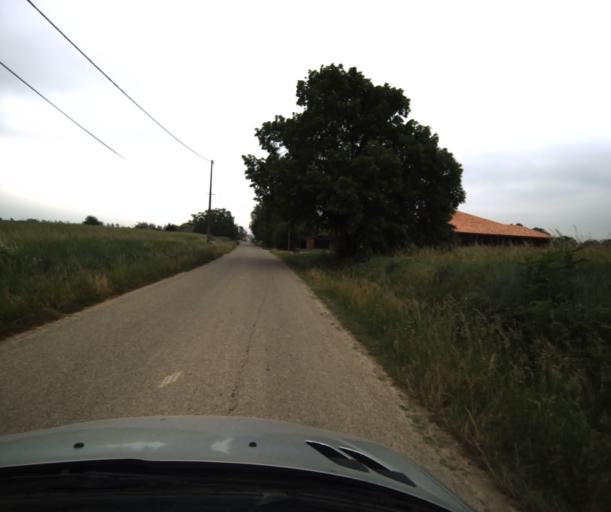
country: FR
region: Midi-Pyrenees
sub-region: Departement du Tarn-et-Garonne
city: Saint-Nicolas-de-la-Grave
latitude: 44.0584
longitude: 0.9745
